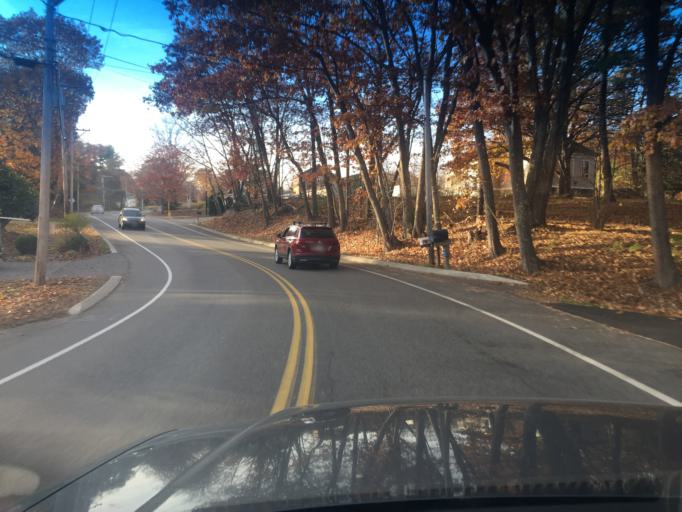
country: US
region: Maine
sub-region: York County
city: York Harbor
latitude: 43.1541
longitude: -70.6814
